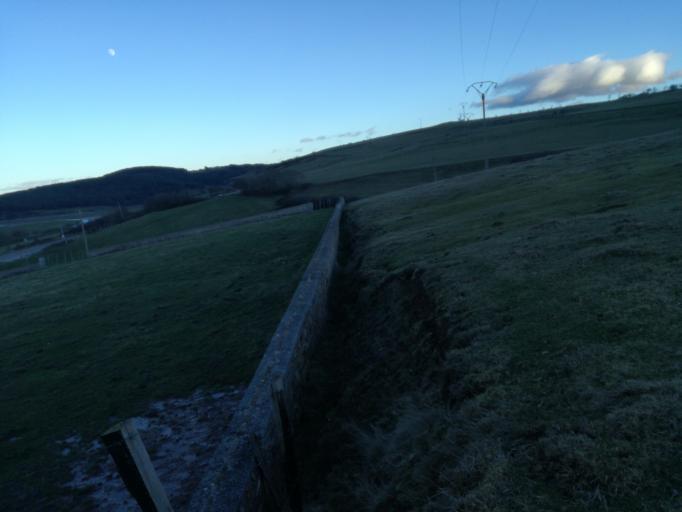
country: ES
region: Cantabria
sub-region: Provincia de Cantabria
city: Reinosa
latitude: 42.9900
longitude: -4.1188
